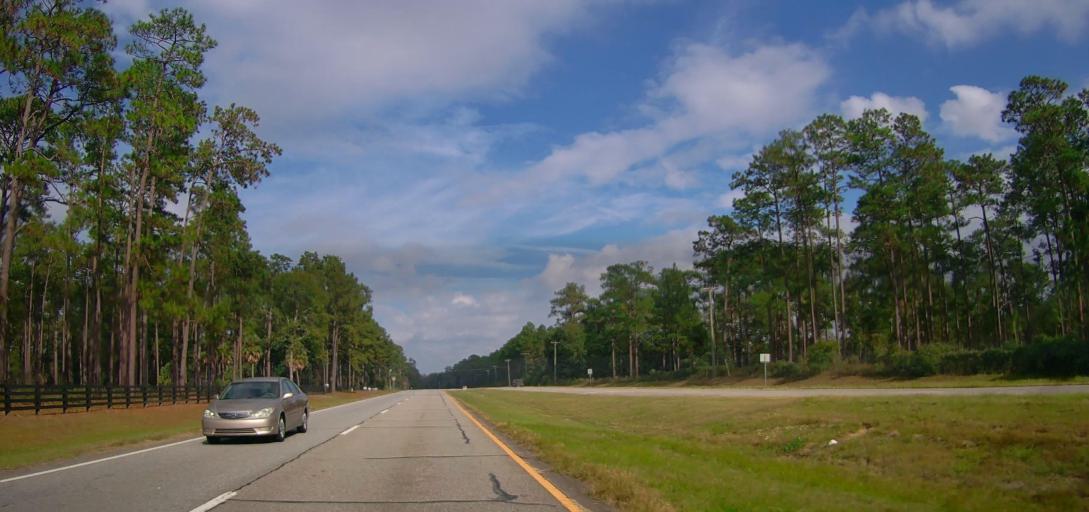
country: US
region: Georgia
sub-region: Thomas County
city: Thomasville
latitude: 30.7874
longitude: -84.0414
